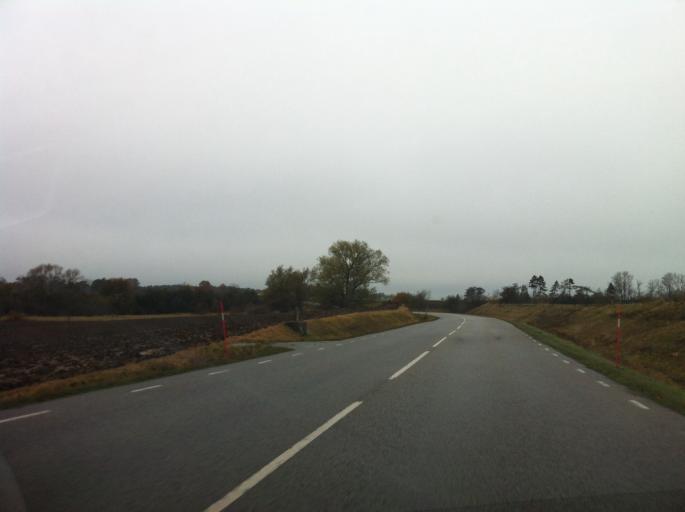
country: SE
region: Skane
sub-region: Kavlinge Kommun
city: Loddekopinge
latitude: 55.8262
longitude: 13.0337
